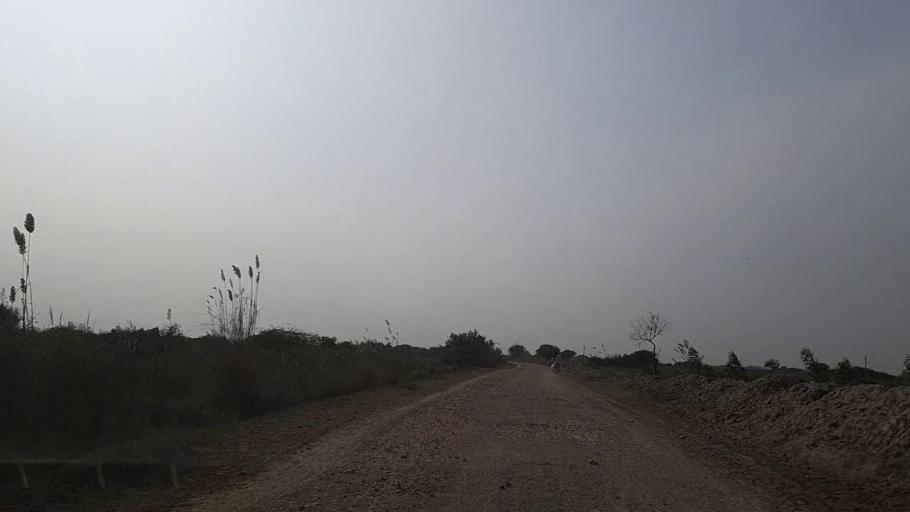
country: PK
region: Sindh
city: Gharo
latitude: 24.6496
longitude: 67.6222
